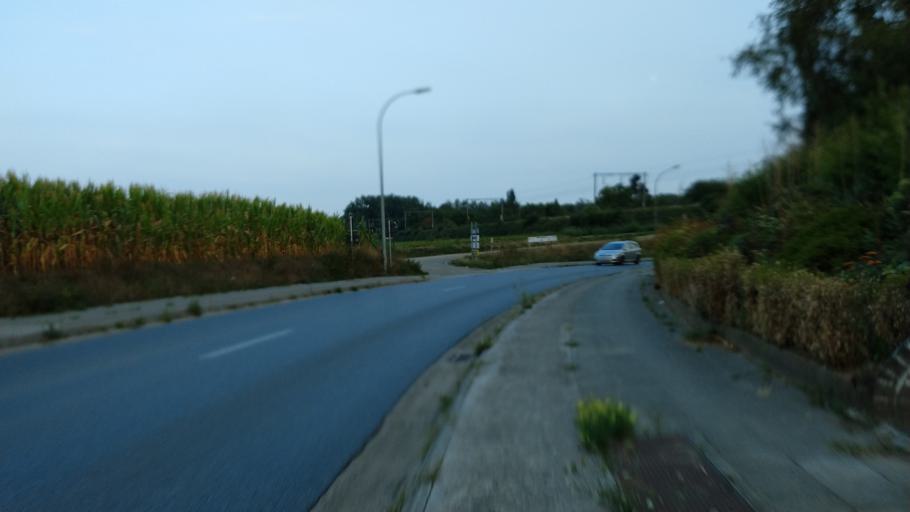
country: BE
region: Flanders
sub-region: Provincie Vlaams-Brabant
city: Bierbeek
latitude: 50.8506
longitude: 4.7906
